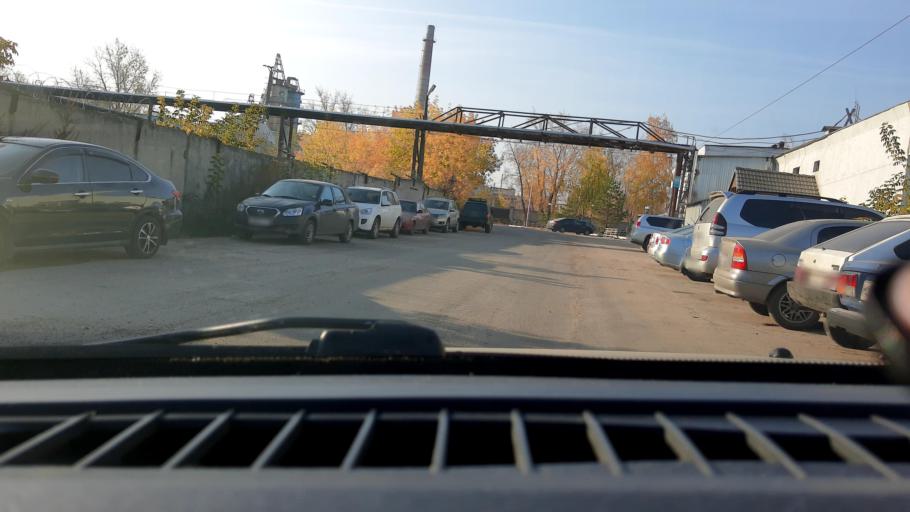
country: RU
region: Nizjnij Novgorod
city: Gorbatovka
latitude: 56.3757
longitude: 43.7885
